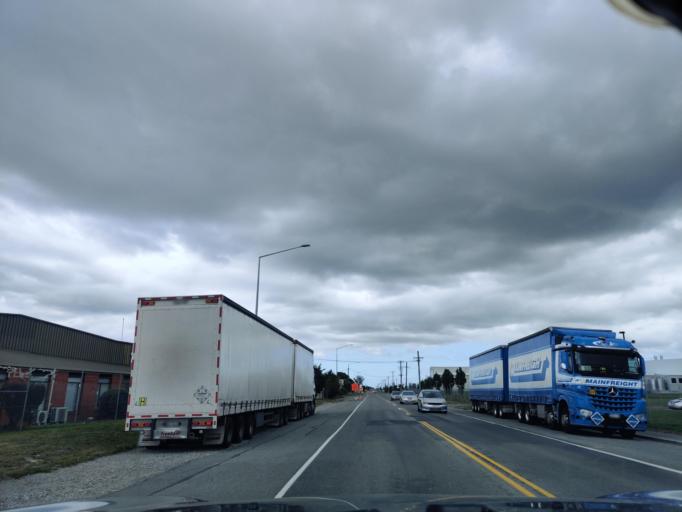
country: NZ
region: Canterbury
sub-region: Selwyn District
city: Prebbleton
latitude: -43.5524
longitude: 172.5154
